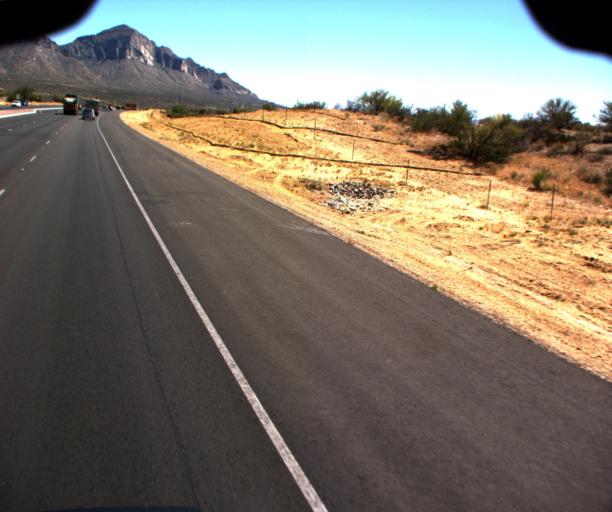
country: US
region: Arizona
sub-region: Pima County
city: Oro Valley
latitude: 32.4325
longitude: -110.9342
